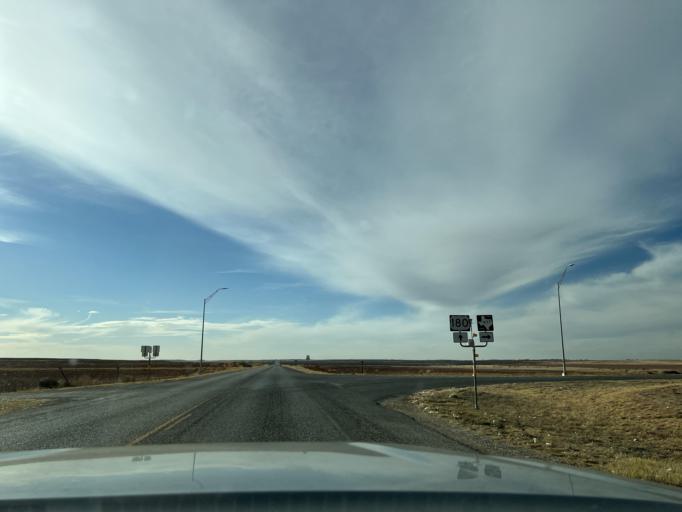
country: US
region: Texas
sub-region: Fisher County
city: Roby
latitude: 32.7406
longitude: -100.4906
